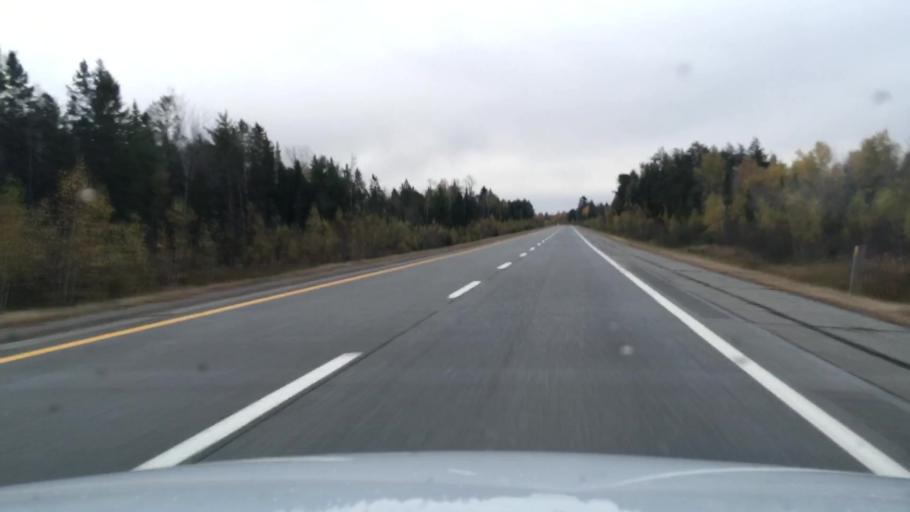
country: US
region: Maine
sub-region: Penobscot County
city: Greenbush
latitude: 45.1081
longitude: -68.6956
